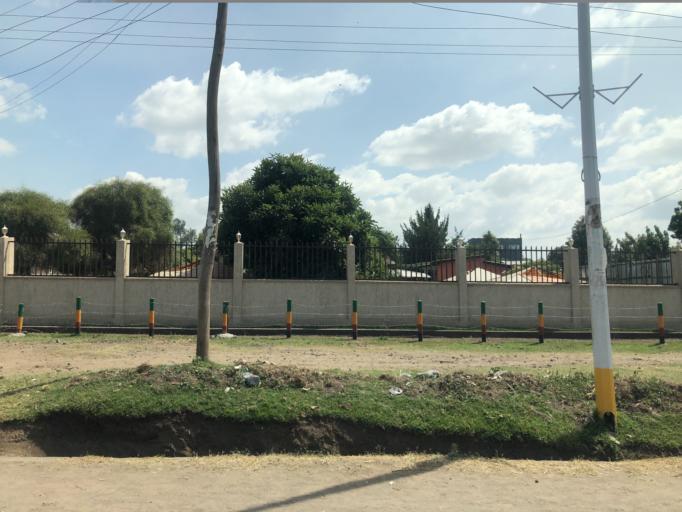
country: ET
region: Oromiya
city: Shashemene
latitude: 7.2081
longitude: 38.6128
